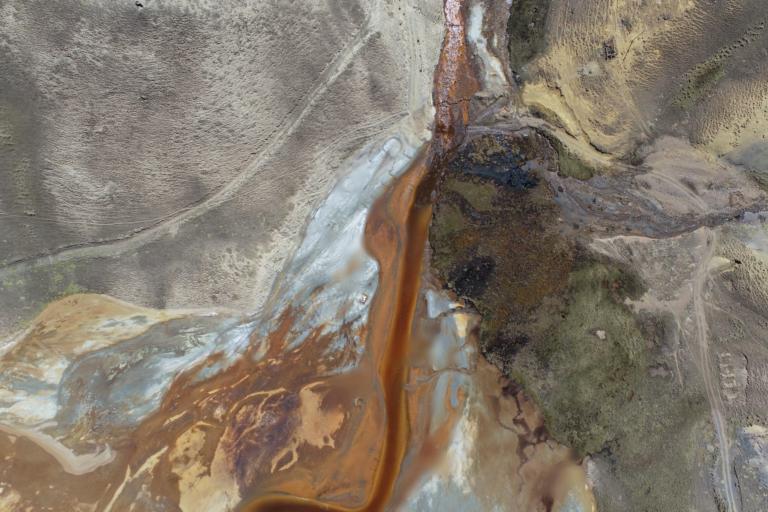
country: BO
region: La Paz
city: La Paz
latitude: -16.3450
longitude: -68.1583
